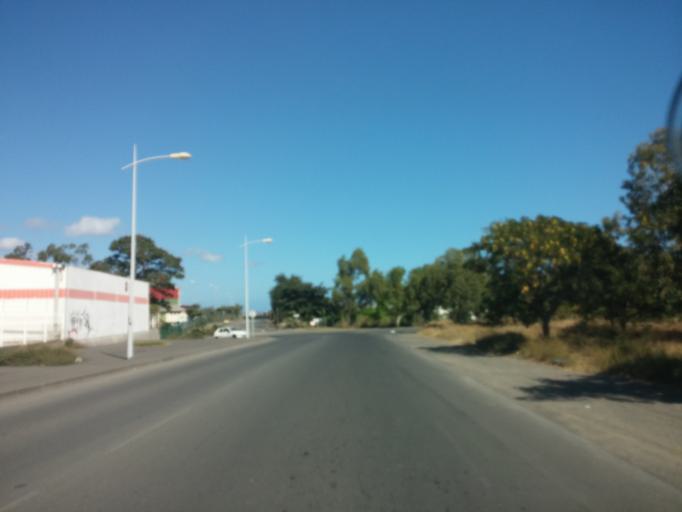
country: RE
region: Reunion
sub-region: Reunion
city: Le Port
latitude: -20.9514
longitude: 55.3013
